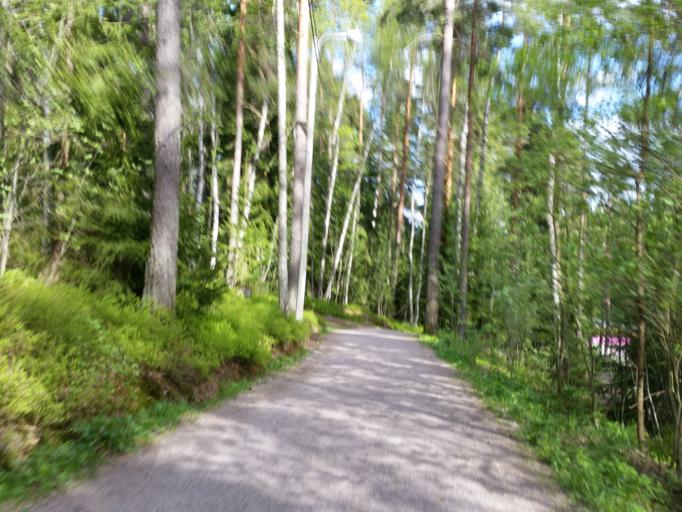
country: FI
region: Uusimaa
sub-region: Helsinki
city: Kauniainen
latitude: 60.1784
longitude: 24.7260
